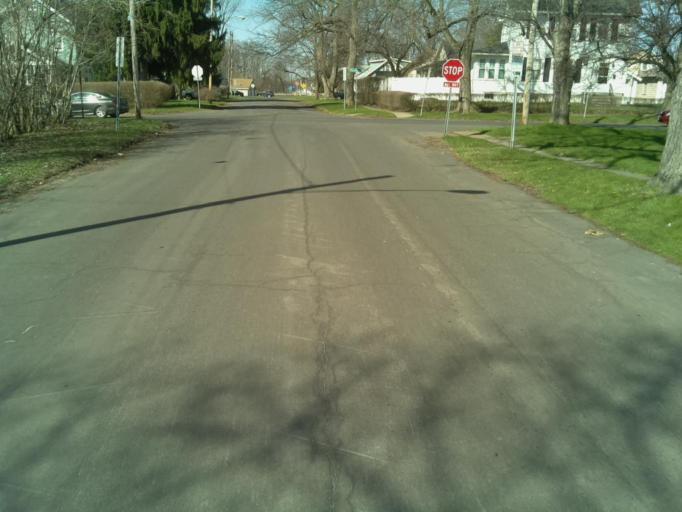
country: US
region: New York
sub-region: Onondaga County
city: Lyncourt
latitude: 43.0592
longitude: -76.1076
